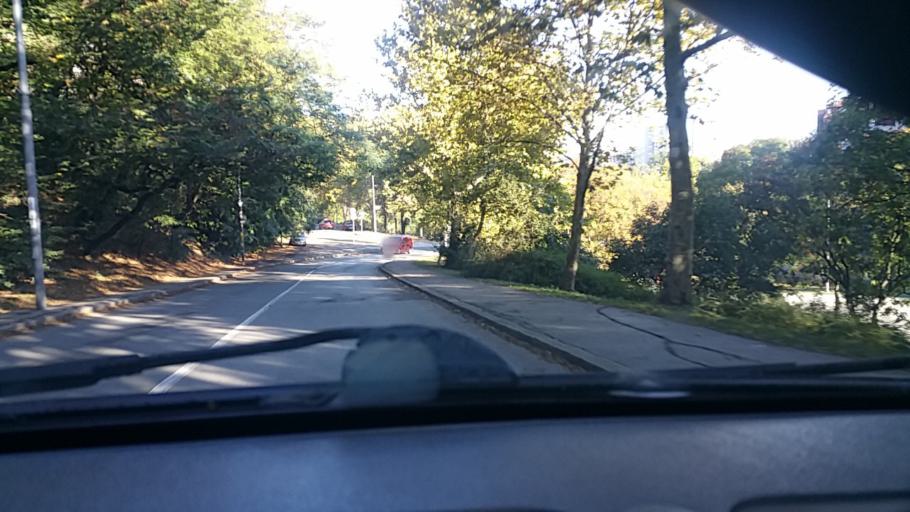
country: RS
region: Central Serbia
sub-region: Belgrade
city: Rakovica
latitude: 44.7466
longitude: 20.4572
